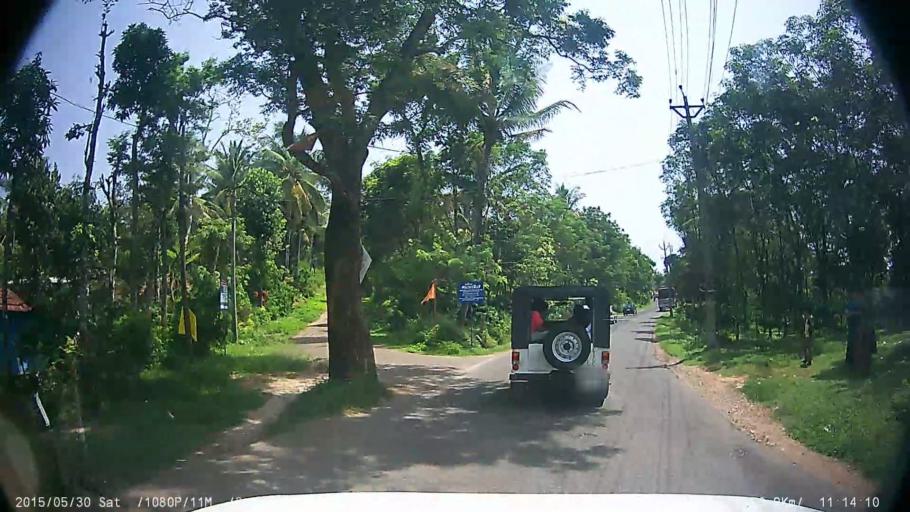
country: IN
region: Kerala
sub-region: Wayanad
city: Panamaram
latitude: 11.7651
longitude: 76.0610
